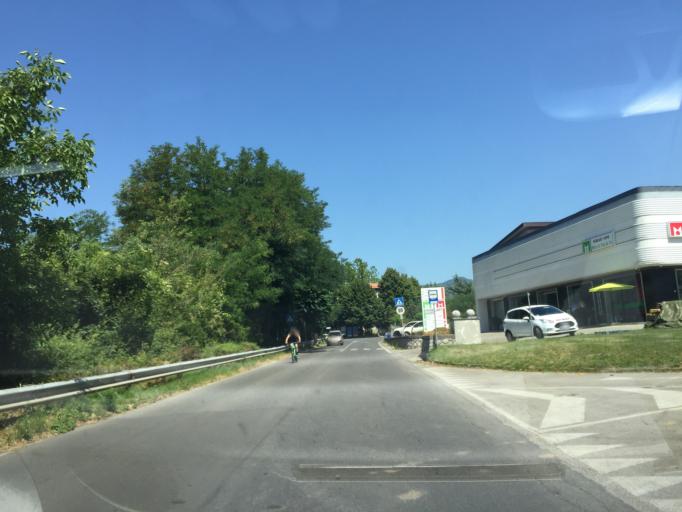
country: IT
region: Tuscany
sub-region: Provincia di Lucca
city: Castelnuovo di Garfagnana
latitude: 44.1194
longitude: 10.4099
